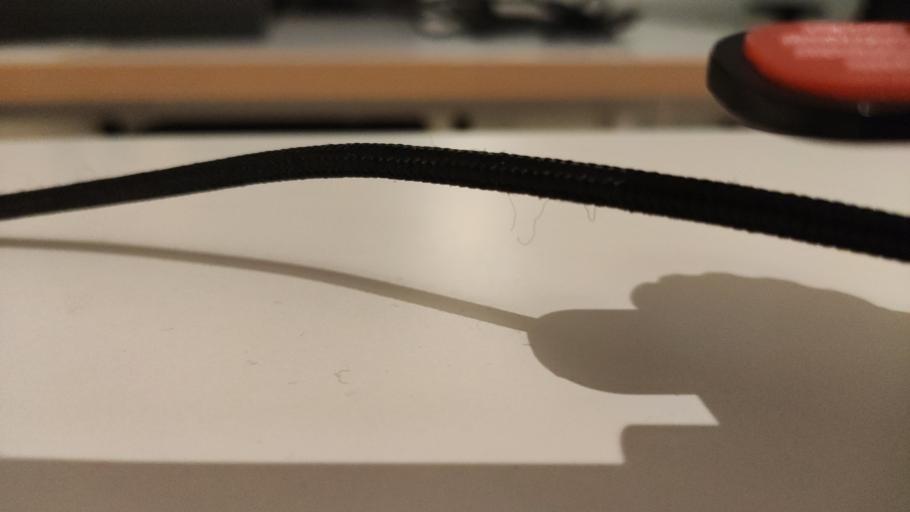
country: RU
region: Moskovskaya
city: Likino-Dulevo
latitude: 55.6676
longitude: 38.9450
